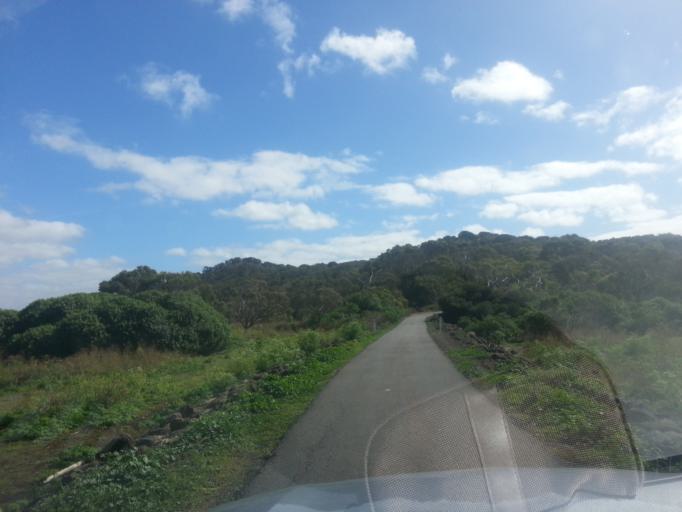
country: AU
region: Victoria
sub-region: Warrnambool
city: Warrnambool
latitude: -38.3271
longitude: 142.3655
